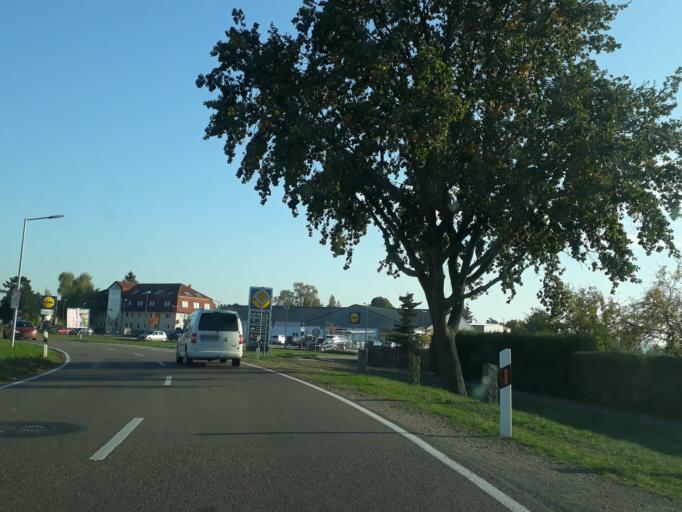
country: DE
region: Saxony
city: Wilsdruff
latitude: 51.0428
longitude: 13.5402
